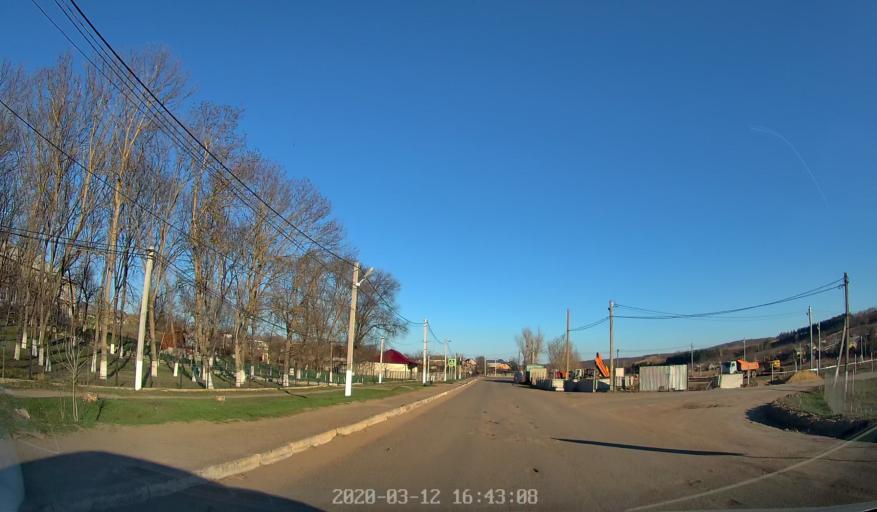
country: MD
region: Anenii Noi
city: Anenii Noi
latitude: 46.8209
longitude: 29.1385
